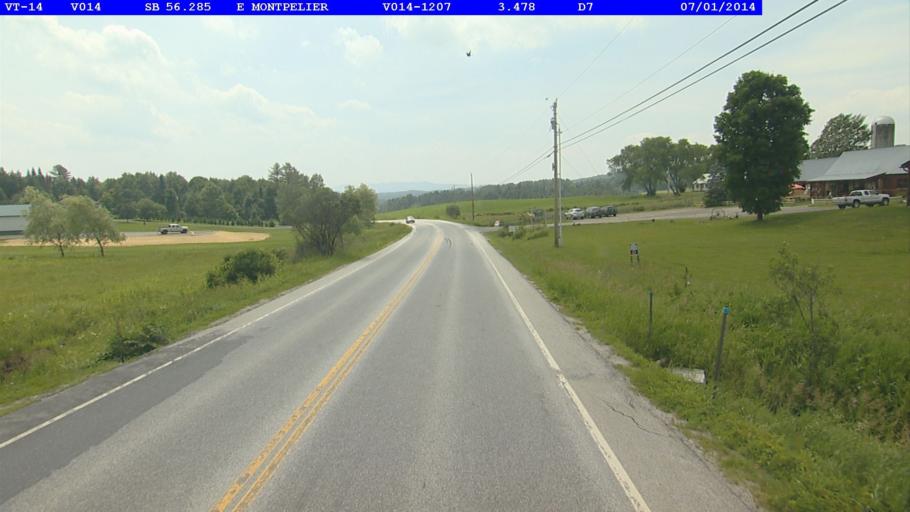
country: US
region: Vermont
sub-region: Washington County
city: Barre
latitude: 44.2813
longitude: -72.4724
